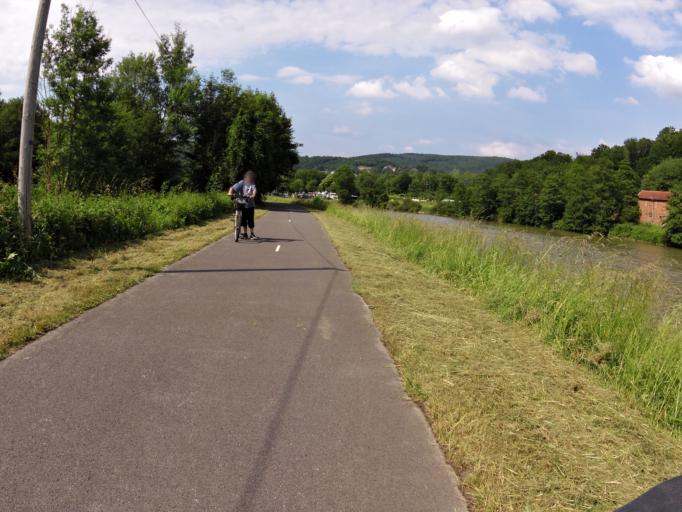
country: FR
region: Champagne-Ardenne
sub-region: Departement des Ardennes
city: Montherme
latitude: 49.8750
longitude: 4.7418
